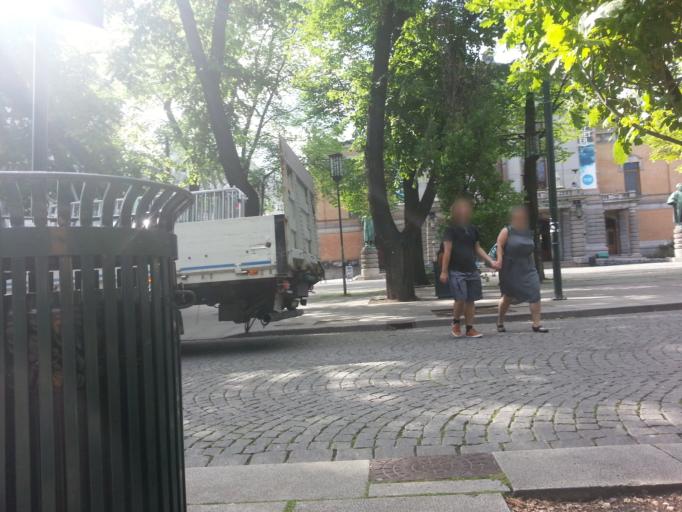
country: NO
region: Oslo
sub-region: Oslo
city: Oslo
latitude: 59.9139
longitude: 10.7357
